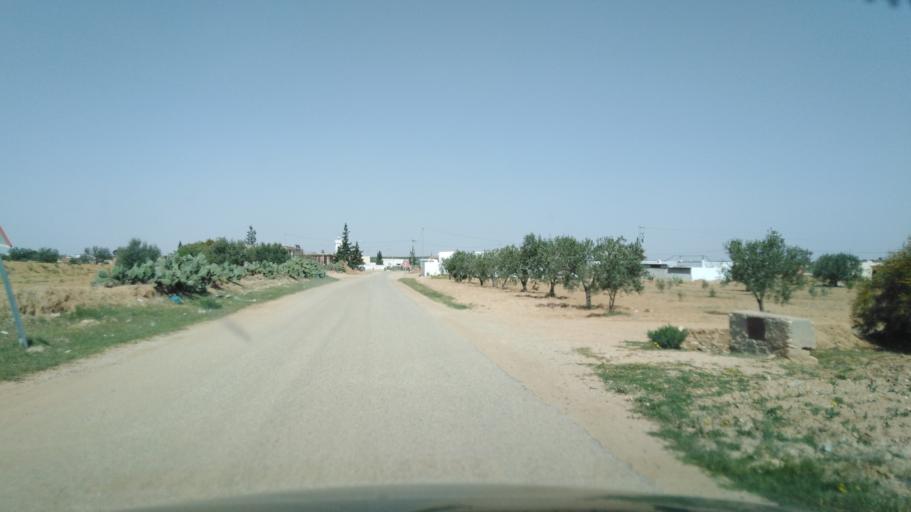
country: TN
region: Safaqis
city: Sfax
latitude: 34.6798
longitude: 10.4366
